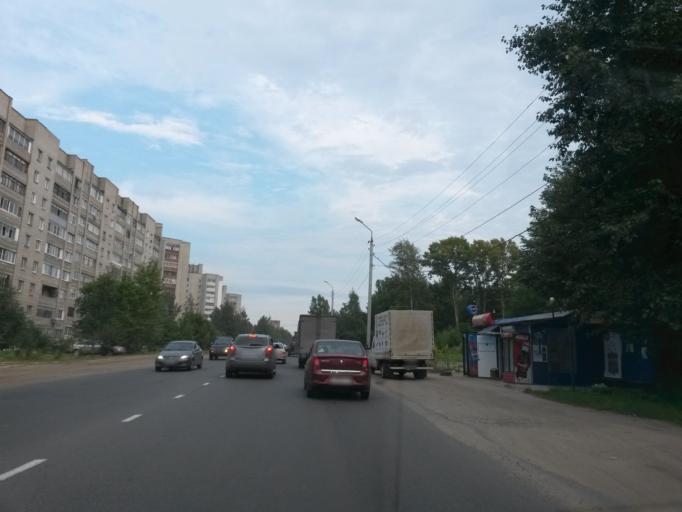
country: RU
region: Jaroslavl
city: Yaroslavl
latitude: 57.5820
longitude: 39.8281
